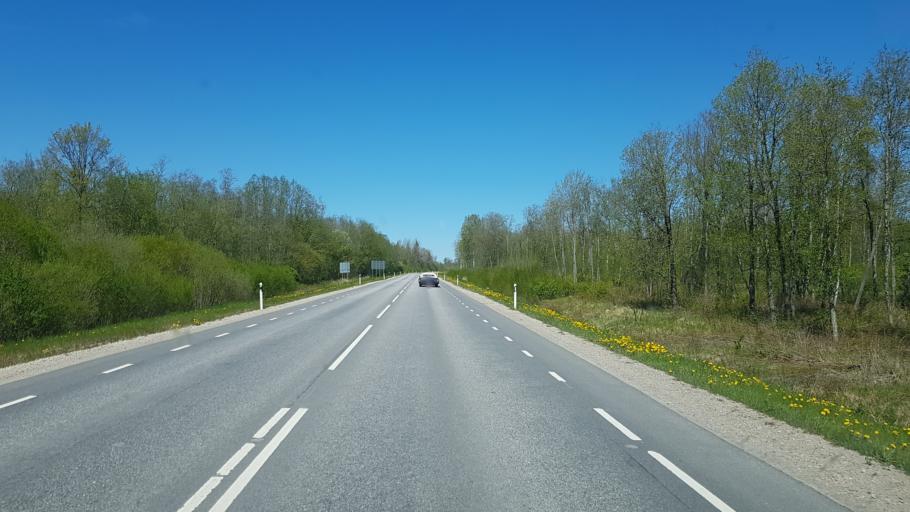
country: EE
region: Viljandimaa
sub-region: Viljandi linn
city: Viljandi
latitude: 58.3784
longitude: 25.5619
